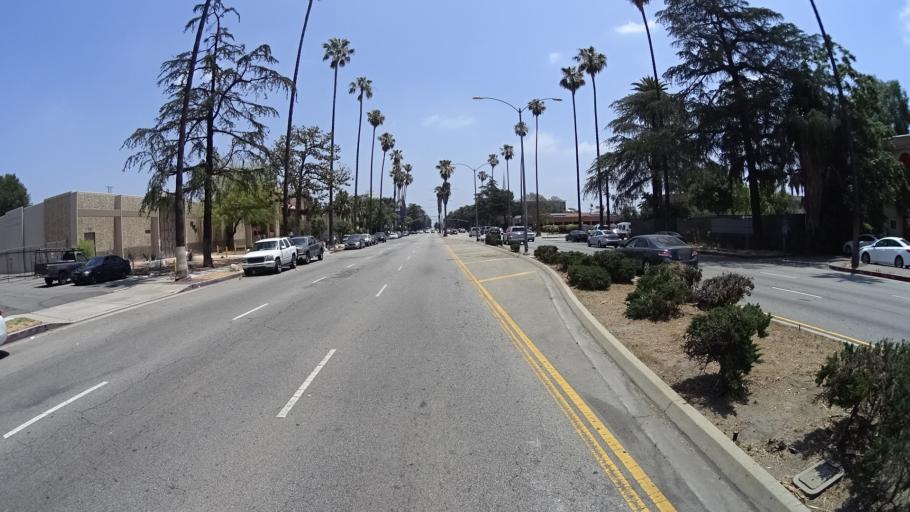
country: US
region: California
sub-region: Los Angeles County
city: Van Nuys
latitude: 34.2012
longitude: -118.4594
